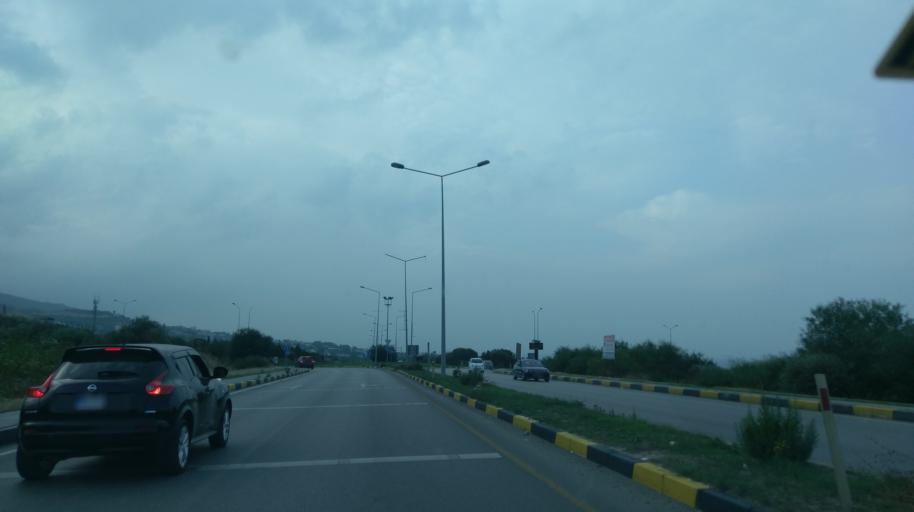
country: CY
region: Keryneia
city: Kyrenia
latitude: 35.3306
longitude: 33.2764
